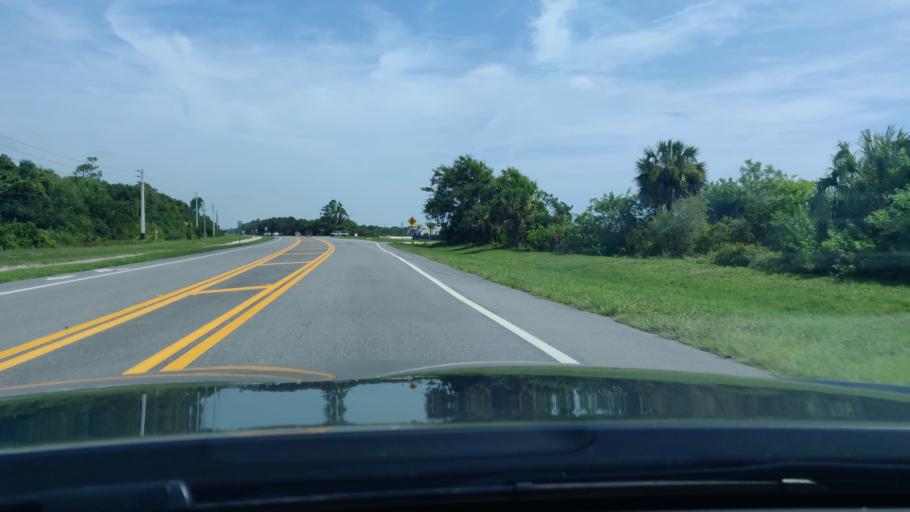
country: US
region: Florida
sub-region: Flagler County
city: Flagler Beach
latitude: 29.4983
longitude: -81.1576
